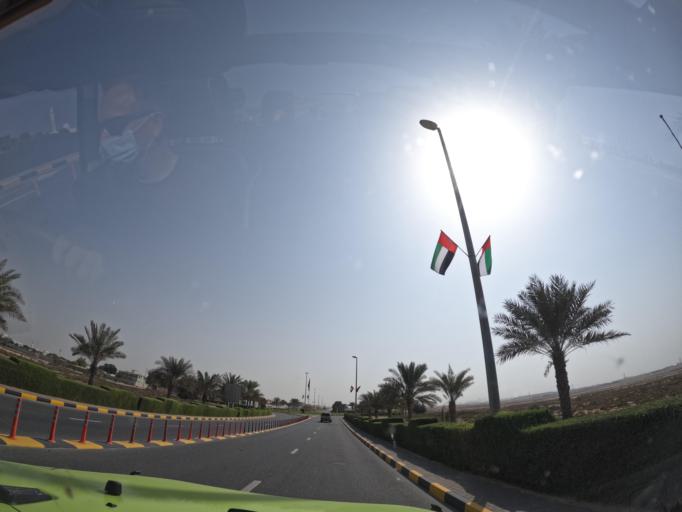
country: AE
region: Umm al Qaywayn
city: Umm al Qaywayn
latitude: 25.4759
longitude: 55.5268
